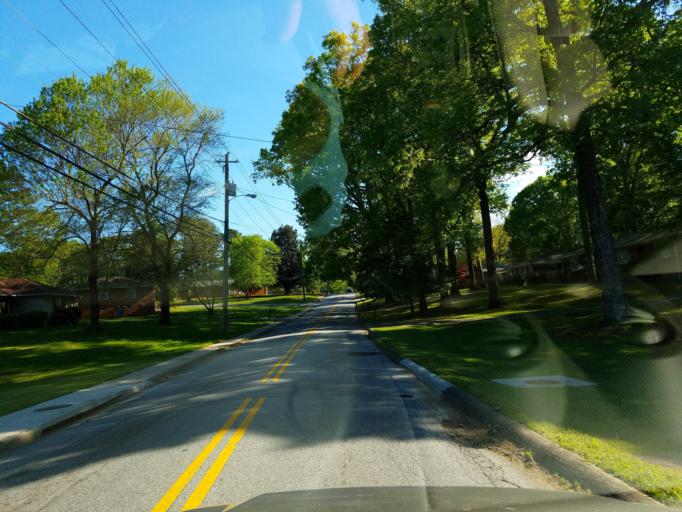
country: US
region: Georgia
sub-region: Cobb County
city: Smyrna
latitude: 33.8599
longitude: -84.5363
